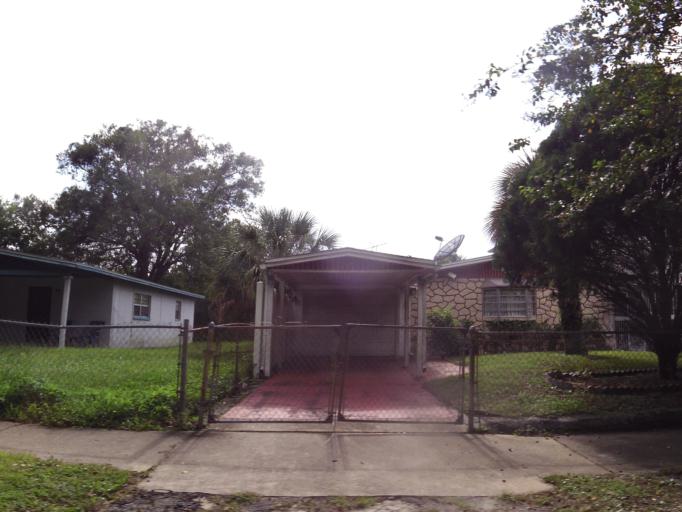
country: US
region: Florida
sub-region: Duval County
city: Jacksonville
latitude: 30.3624
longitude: -81.6883
